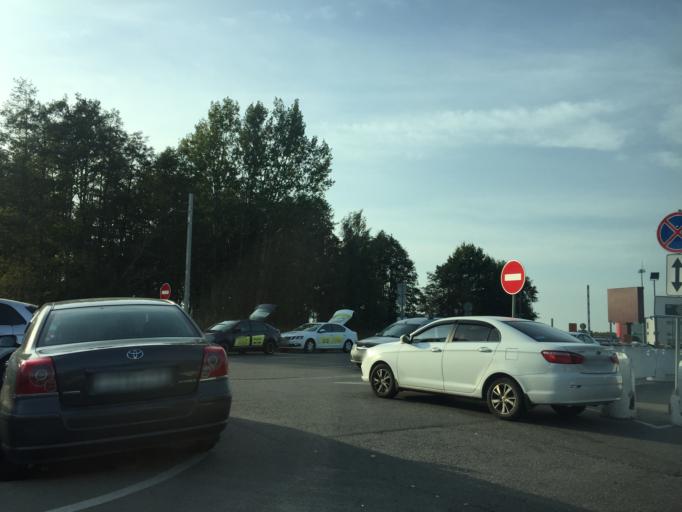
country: RU
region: Kaliningrad
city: Gur'yevsk
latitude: 54.8803
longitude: 20.5871
